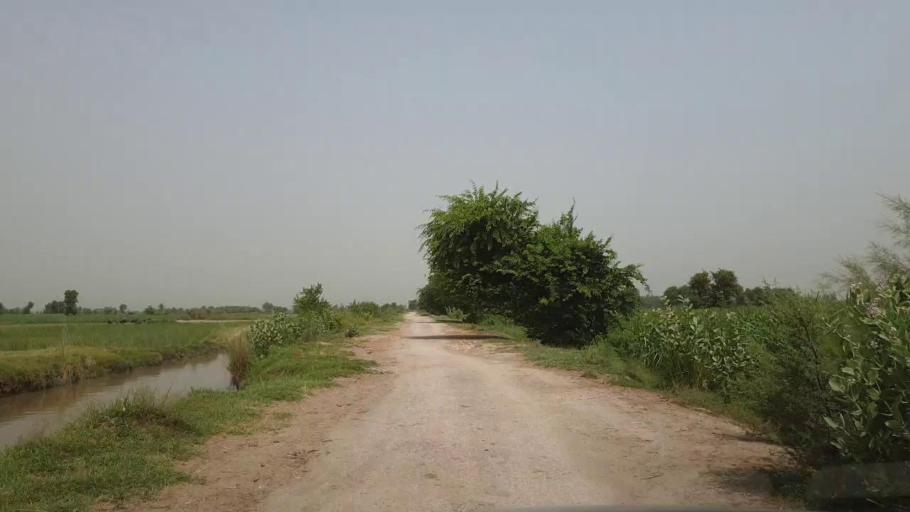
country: PK
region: Sindh
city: Gambat
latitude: 27.4516
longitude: 68.4421
